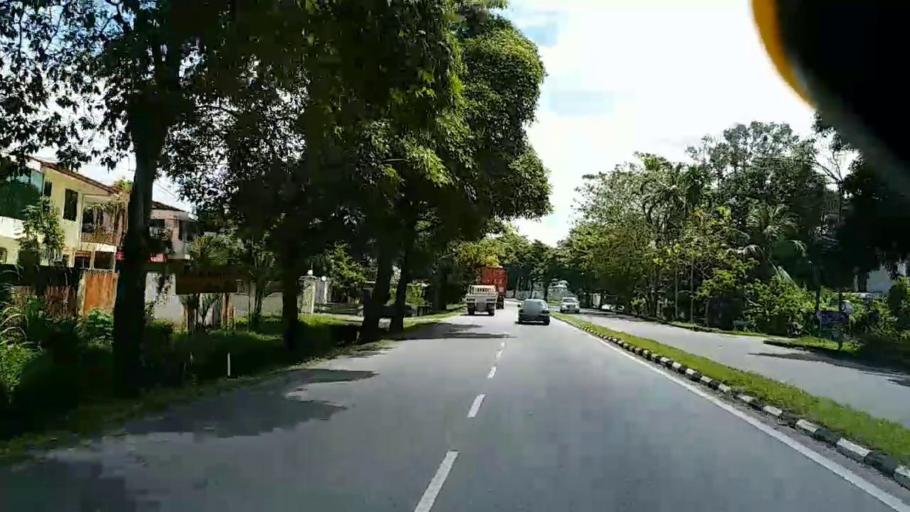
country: MY
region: Sarawak
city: Sibu
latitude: 2.3025
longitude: 111.8349
